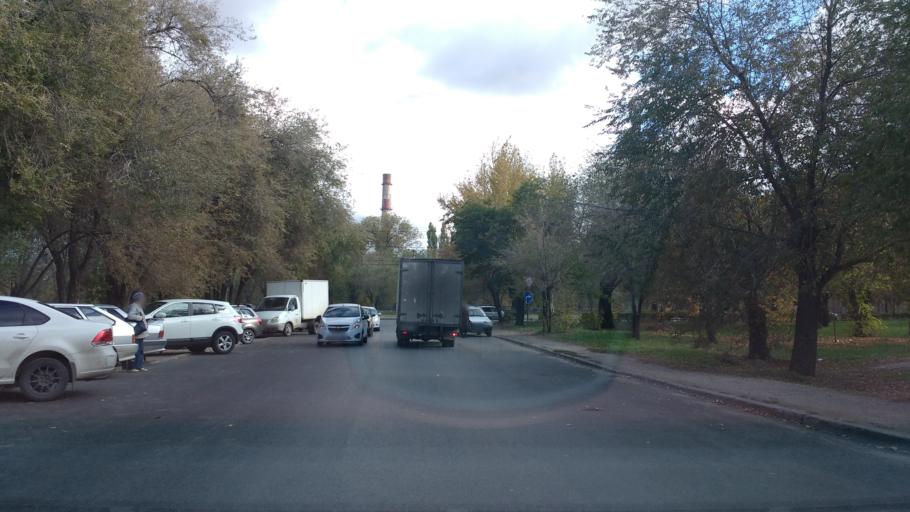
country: RU
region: Volgograd
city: Krasnoslobodsk
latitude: 48.7535
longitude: 44.5499
